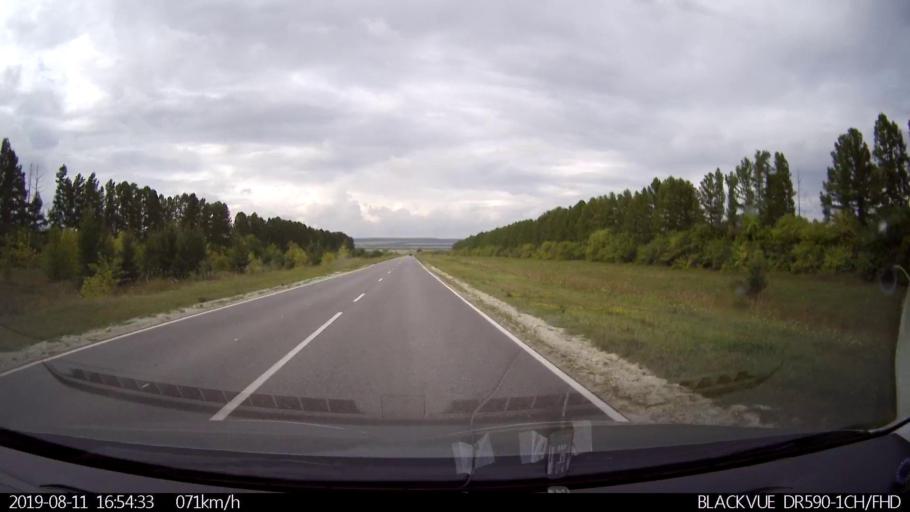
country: RU
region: Ulyanovsk
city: Mayna
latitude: 54.2739
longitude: 47.6661
